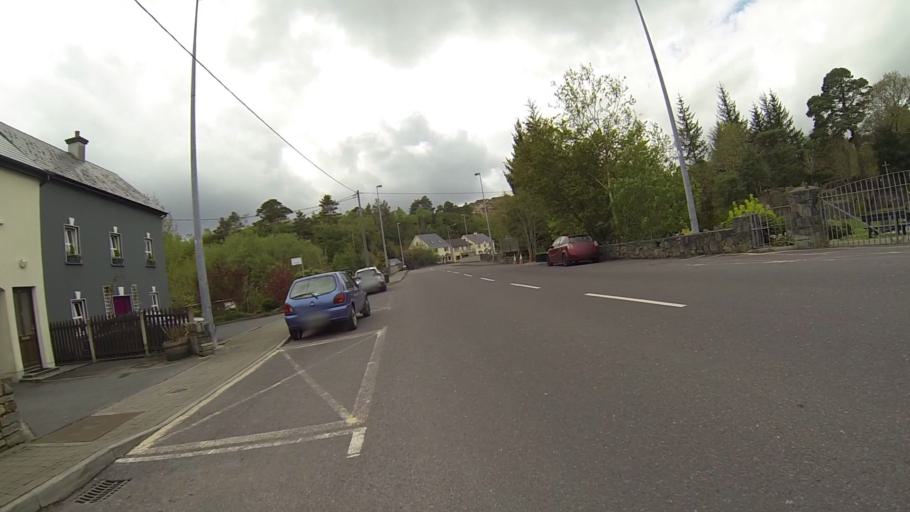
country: IE
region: Munster
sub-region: County Cork
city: Bantry
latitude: 51.7496
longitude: -9.5527
